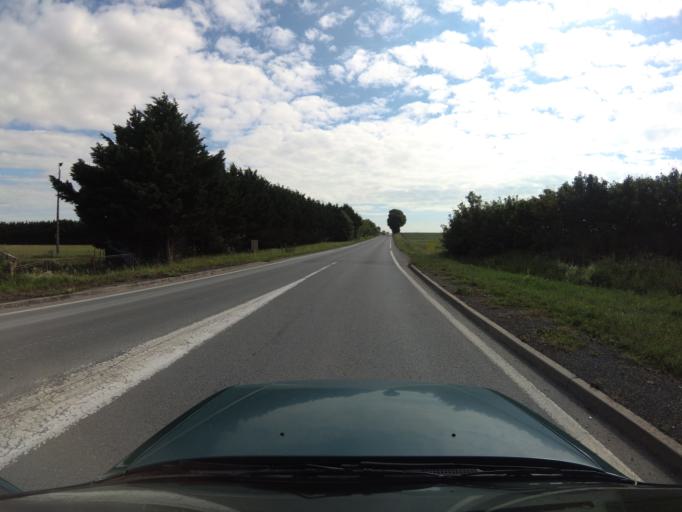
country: FR
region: Poitou-Charentes
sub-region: Departement de la Charente-Maritime
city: Saint-Xandre
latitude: 46.2341
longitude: -1.0741
